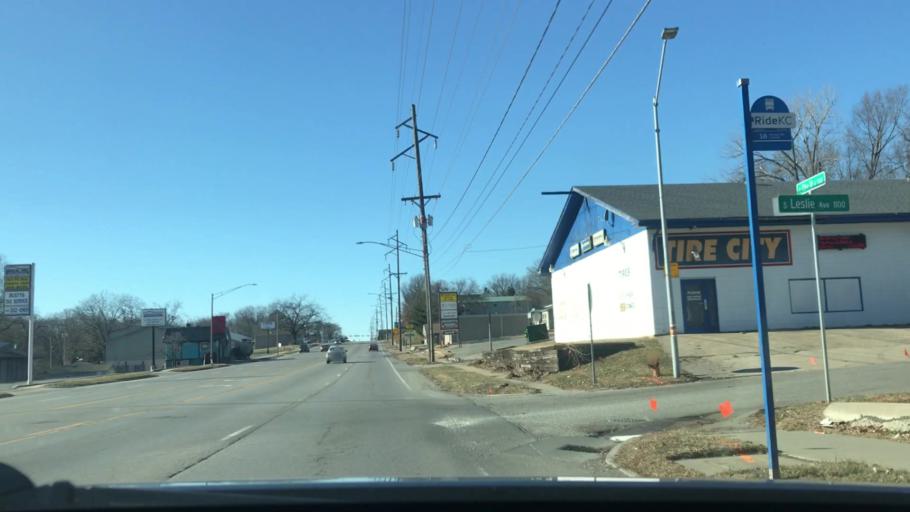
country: US
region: Missouri
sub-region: Jackson County
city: Independence
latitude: 39.0790
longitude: -94.4068
